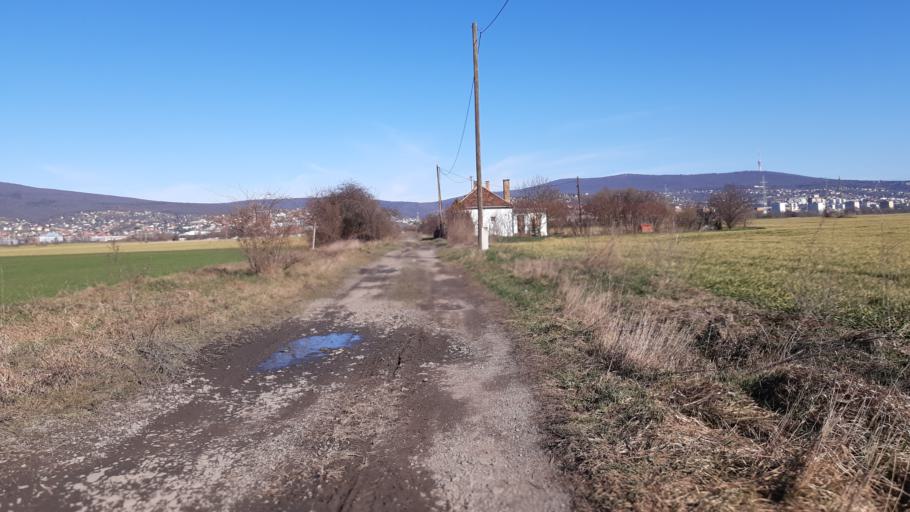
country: HU
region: Baranya
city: Pellerd
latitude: 46.0490
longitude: 18.1881
